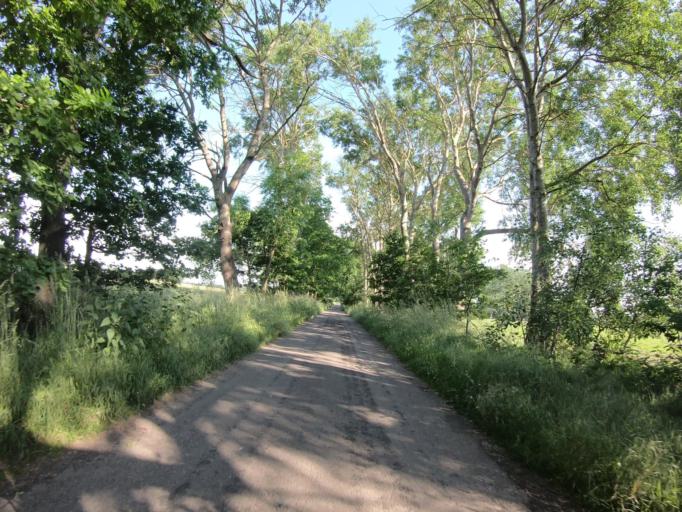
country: DE
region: Lower Saxony
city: Wasbuttel
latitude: 52.4115
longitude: 10.6065
